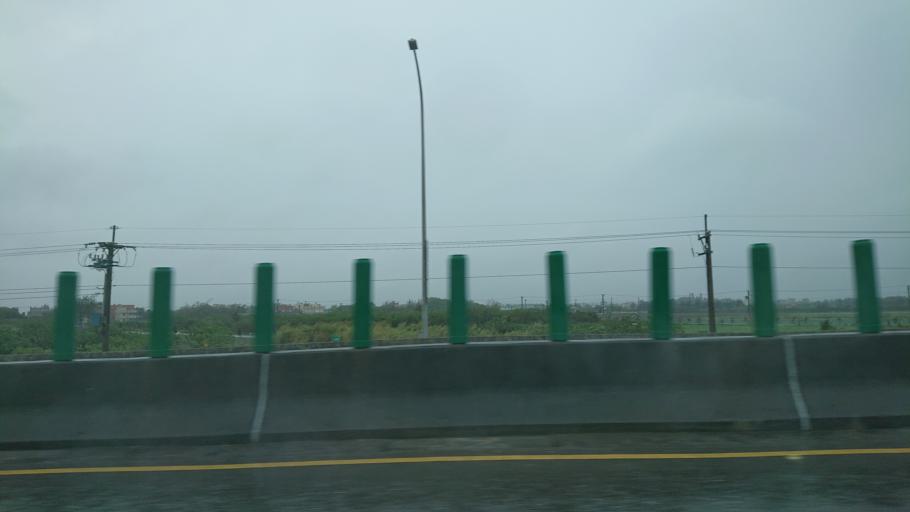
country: TW
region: Taiwan
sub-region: Chiayi
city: Taibao
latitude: 23.7348
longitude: 120.2320
